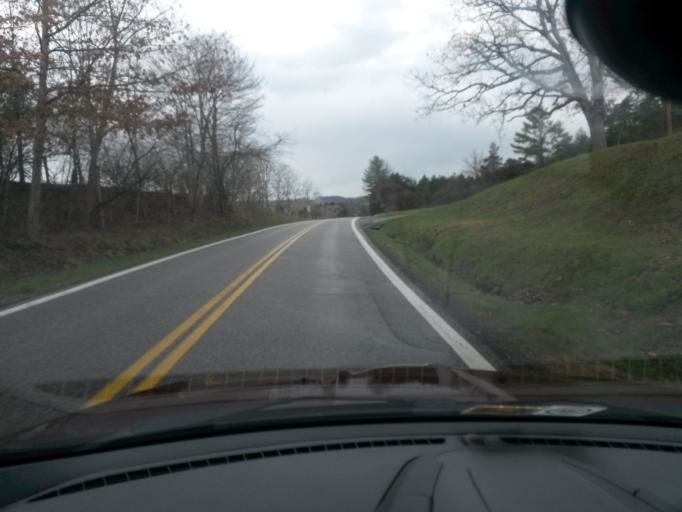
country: US
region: Virginia
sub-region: Bath County
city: Warm Springs
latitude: 38.0450
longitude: -79.6871
